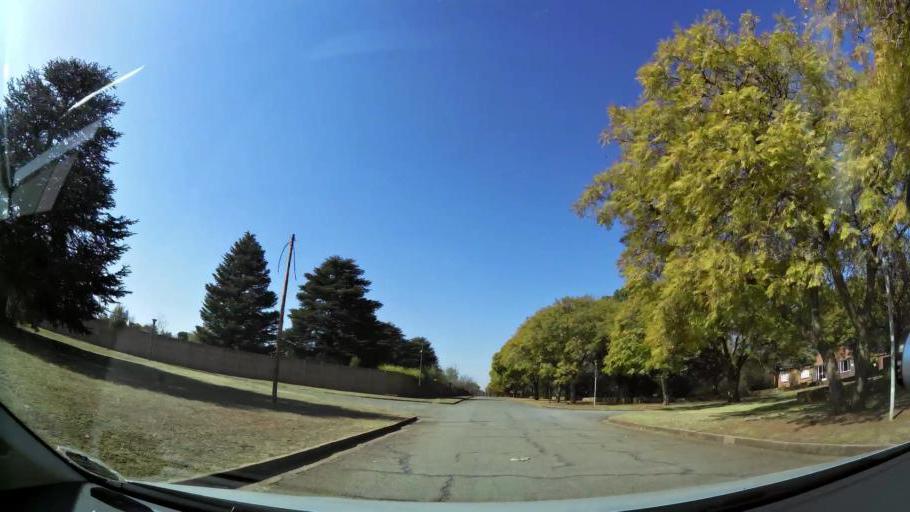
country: ZA
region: Gauteng
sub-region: Ekurhuleni Metropolitan Municipality
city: Tembisa
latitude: -26.0385
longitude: 28.2454
